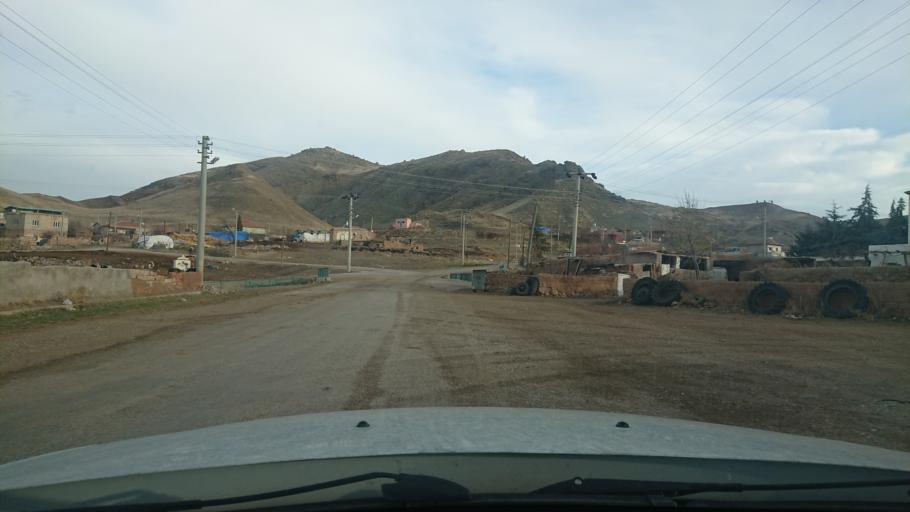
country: TR
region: Aksaray
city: Acipinar
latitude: 38.6176
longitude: 33.7845
